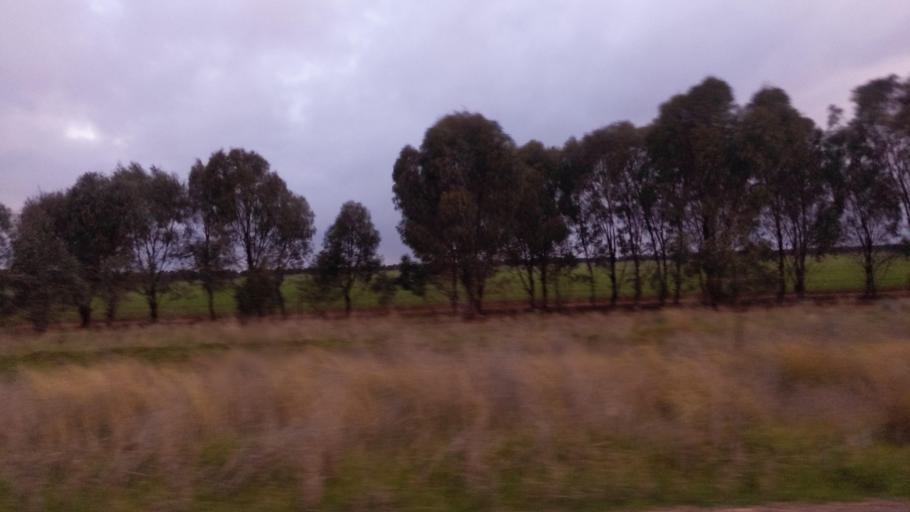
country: AU
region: New South Wales
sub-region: Coolamon
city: Coolamon
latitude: -34.7629
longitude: 146.8961
